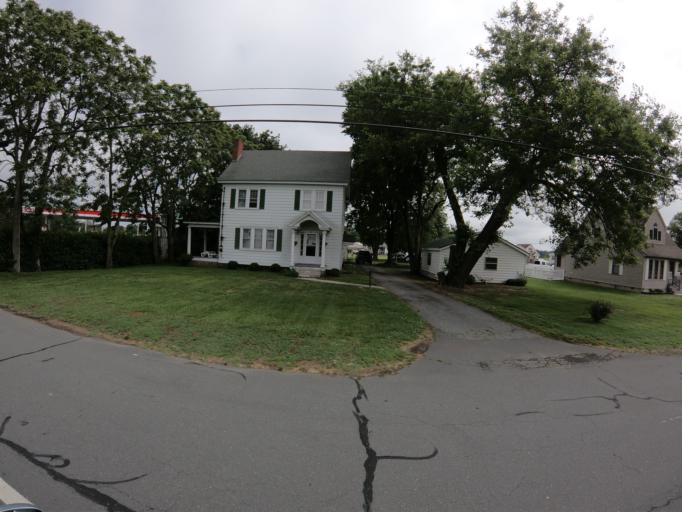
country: US
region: Delaware
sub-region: Kent County
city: Felton
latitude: 39.0065
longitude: -75.5681
